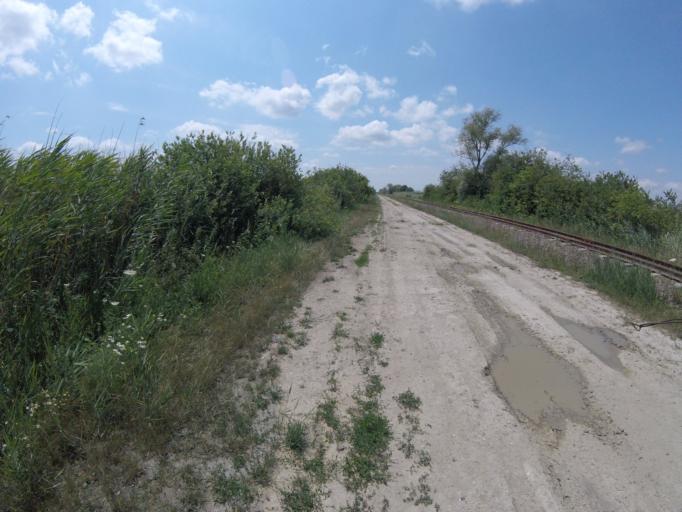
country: HU
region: Hajdu-Bihar
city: Hortobagy
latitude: 47.6450
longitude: 21.0874
